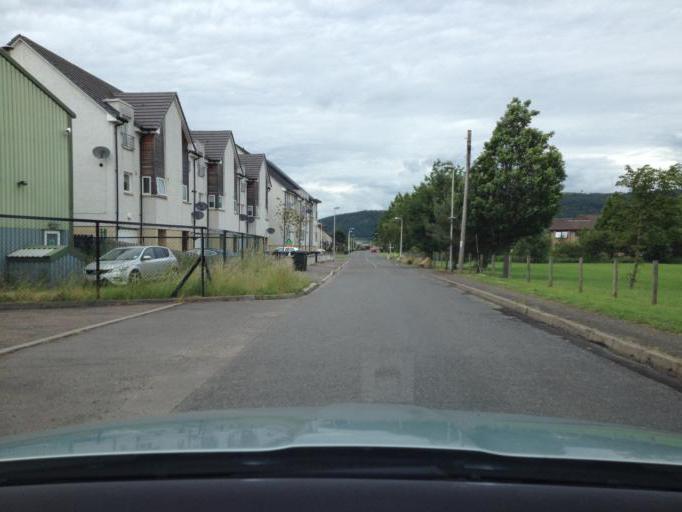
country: GB
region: Scotland
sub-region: Perth and Kinross
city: Bridge of Earn
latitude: 56.3409
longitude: -3.4014
